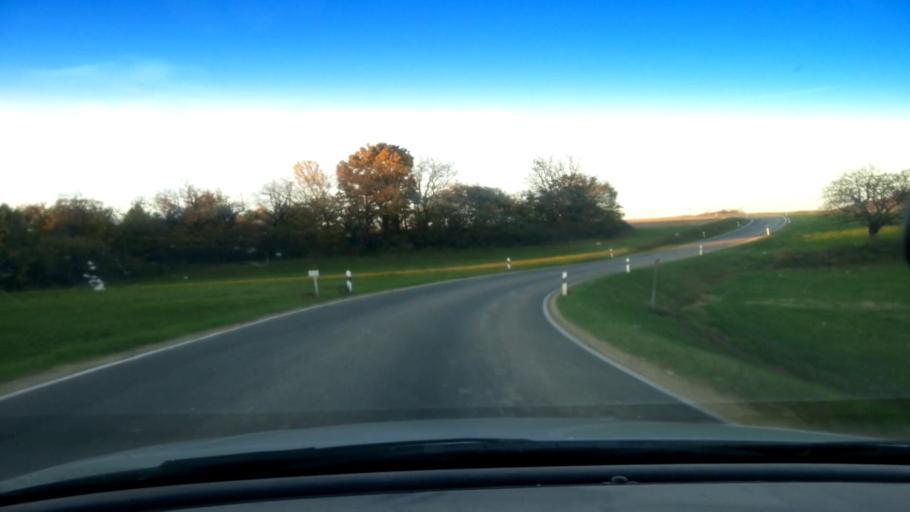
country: DE
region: Bavaria
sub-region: Upper Franconia
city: Heiligenstadt
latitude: 49.8524
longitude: 11.1164
